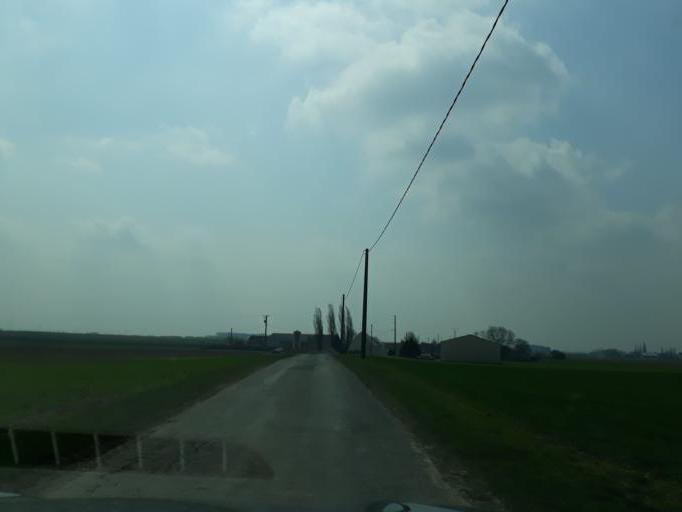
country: FR
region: Centre
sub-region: Departement d'Eure-et-Loir
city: Baigneaux
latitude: 48.0938
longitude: 1.8214
